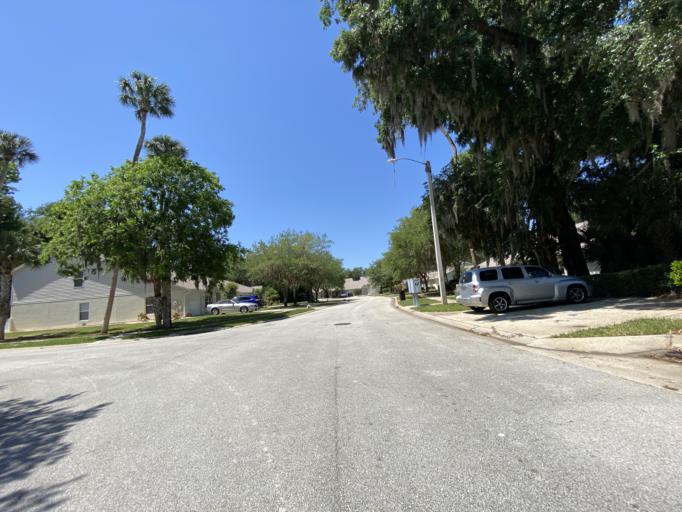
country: US
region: Florida
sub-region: Volusia County
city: South Daytona
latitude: 29.1507
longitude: -81.0067
